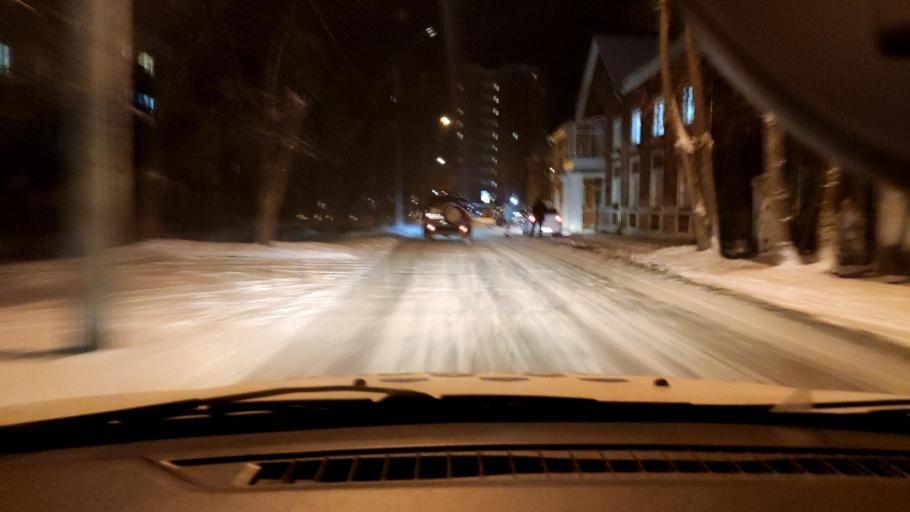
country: RU
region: Perm
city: Kultayevo
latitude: 58.0049
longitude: 55.9633
